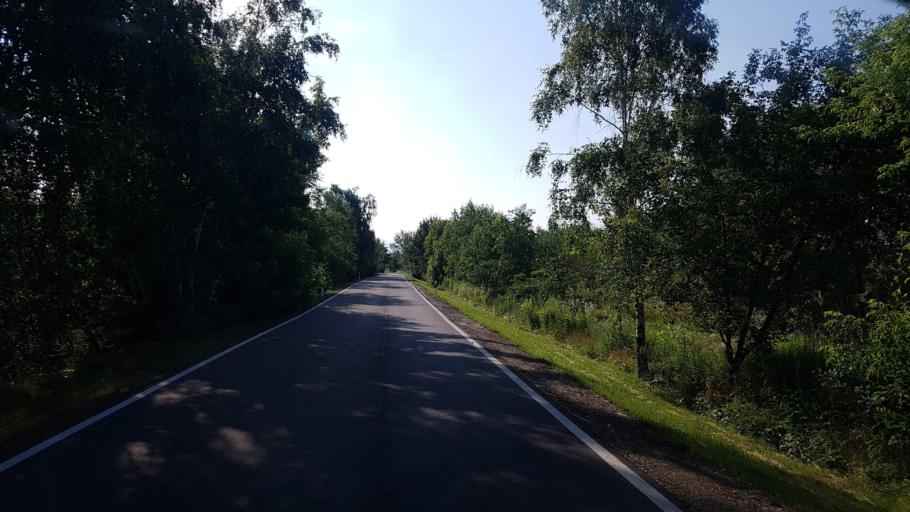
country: DE
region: Brandenburg
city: Grossraschen
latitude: 51.5773
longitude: 14.0201
